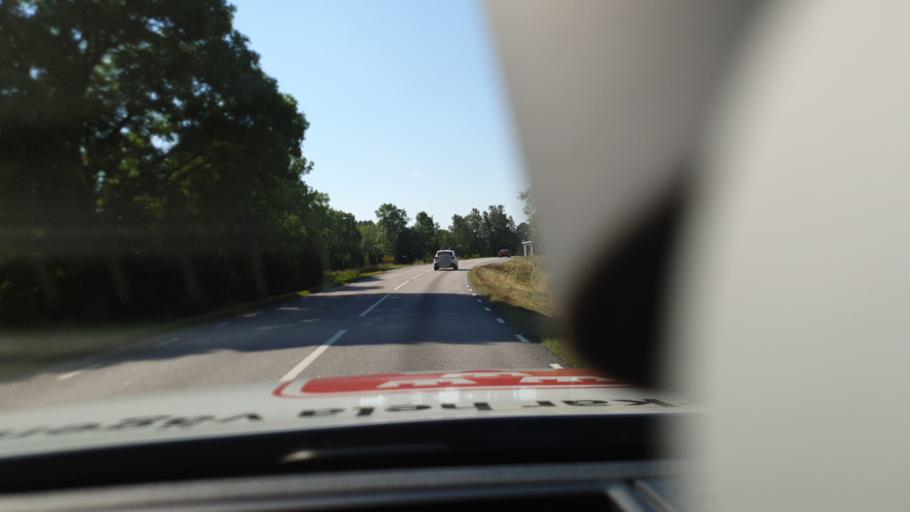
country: SE
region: Stockholm
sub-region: Norrtalje Kommun
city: Arno
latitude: 60.0095
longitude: 18.8027
